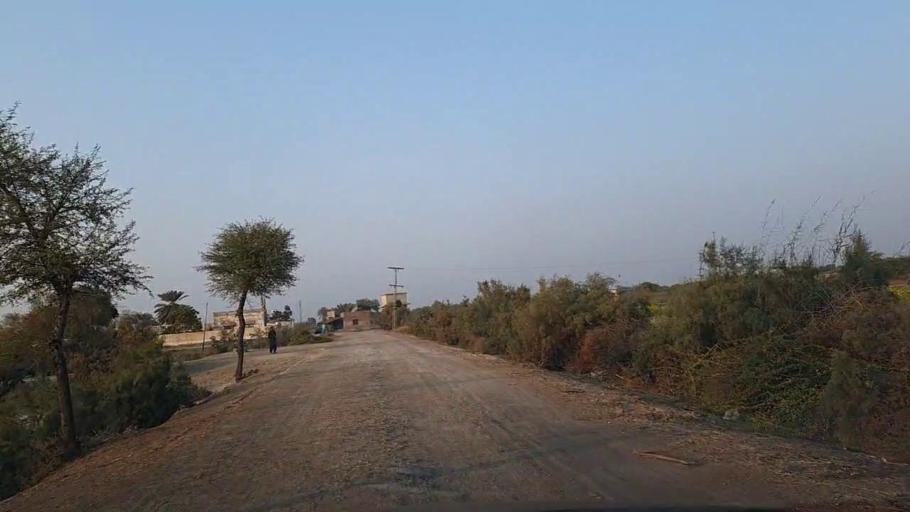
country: PK
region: Sindh
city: Daur
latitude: 26.4338
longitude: 68.3873
